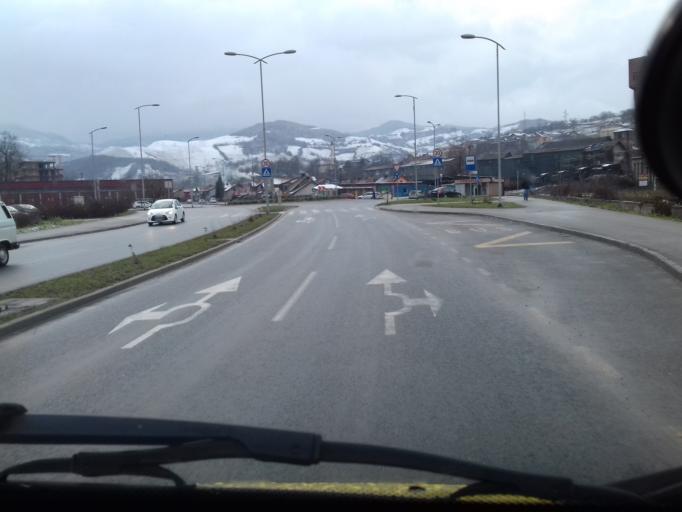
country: BA
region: Federation of Bosnia and Herzegovina
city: Zenica
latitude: 44.2080
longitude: 17.9021
